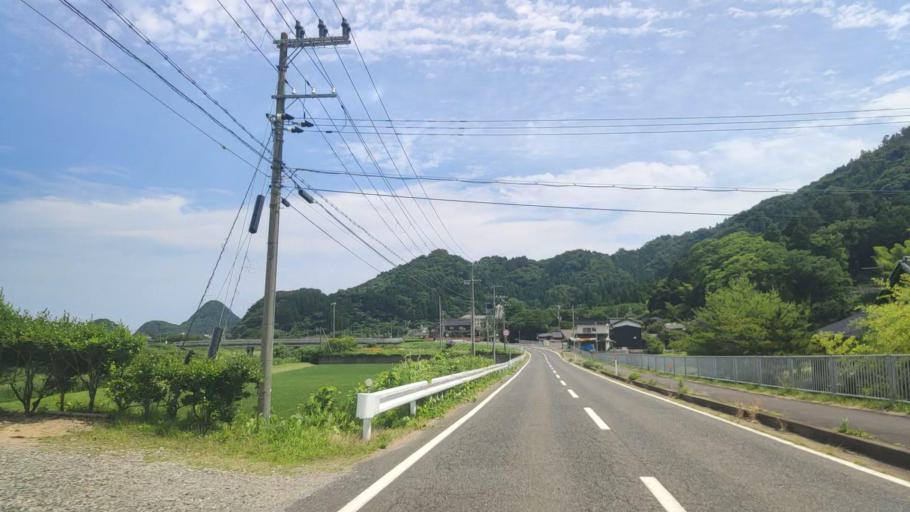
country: JP
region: Hyogo
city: Toyooka
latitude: 35.6460
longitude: 134.7628
